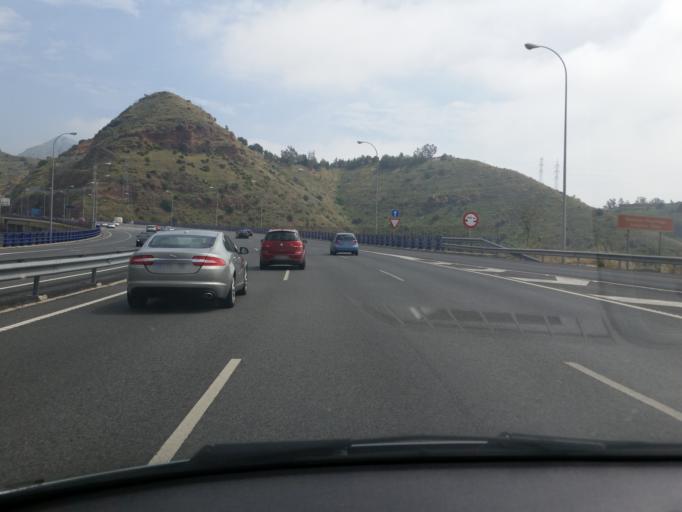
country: ES
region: Andalusia
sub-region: Provincia de Malaga
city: Malaga
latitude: 36.7383
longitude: -4.3930
